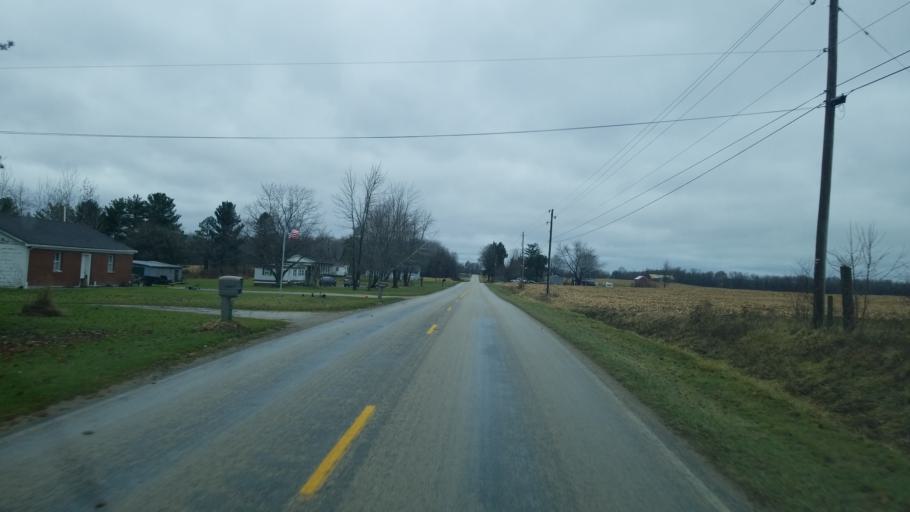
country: US
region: Ohio
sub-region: Ashtabula County
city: Andover
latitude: 41.6422
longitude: -80.6155
